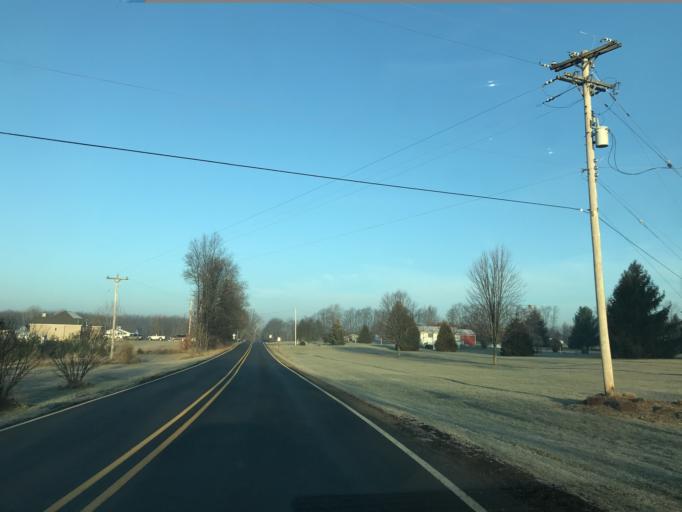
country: US
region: Michigan
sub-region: Ingham County
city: Leslie
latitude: 42.4264
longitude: -84.5263
